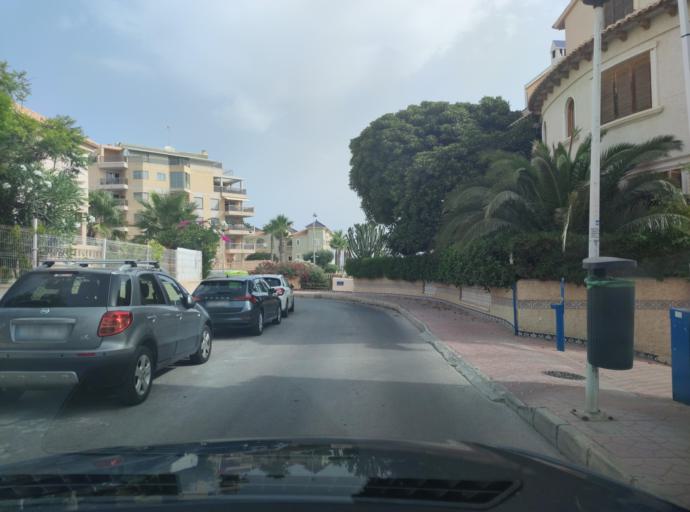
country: ES
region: Valencia
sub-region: Provincia de Alicante
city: Guardamar del Segura
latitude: 38.0648
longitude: -0.6525
